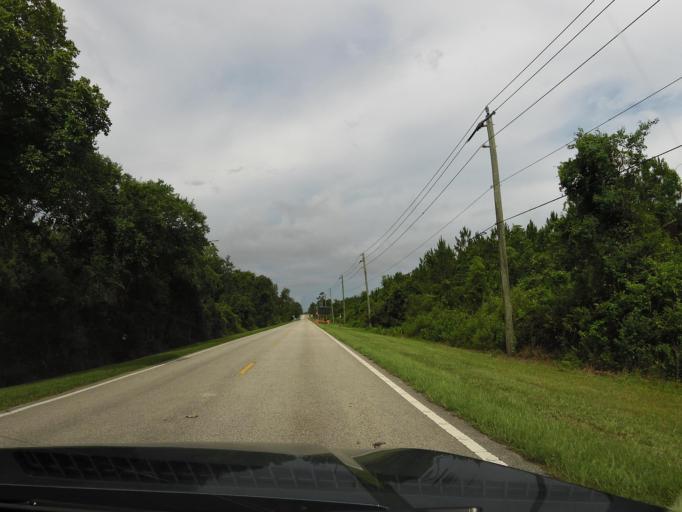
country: US
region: Florida
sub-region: Saint Johns County
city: Saint Augustine South
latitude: 29.8605
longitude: -81.4032
